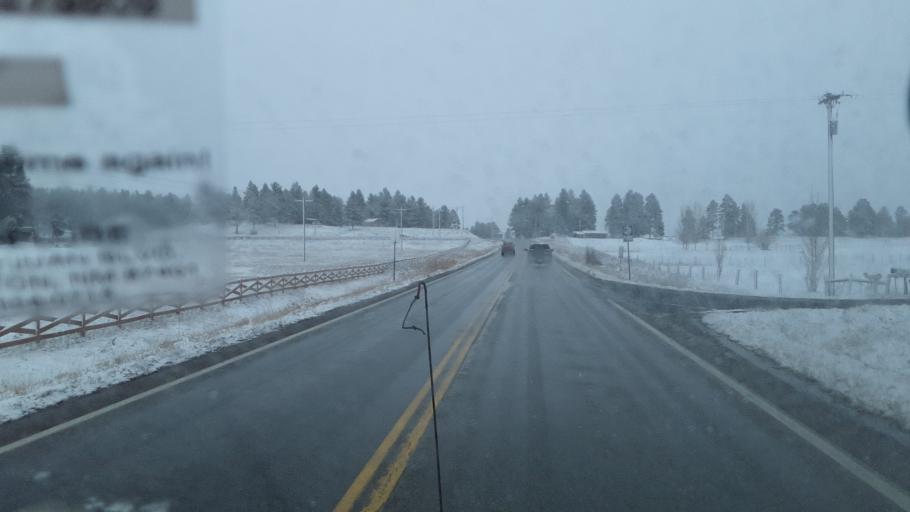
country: US
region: Colorado
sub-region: Archuleta County
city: Pagosa Springs
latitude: 37.2296
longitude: -106.9850
